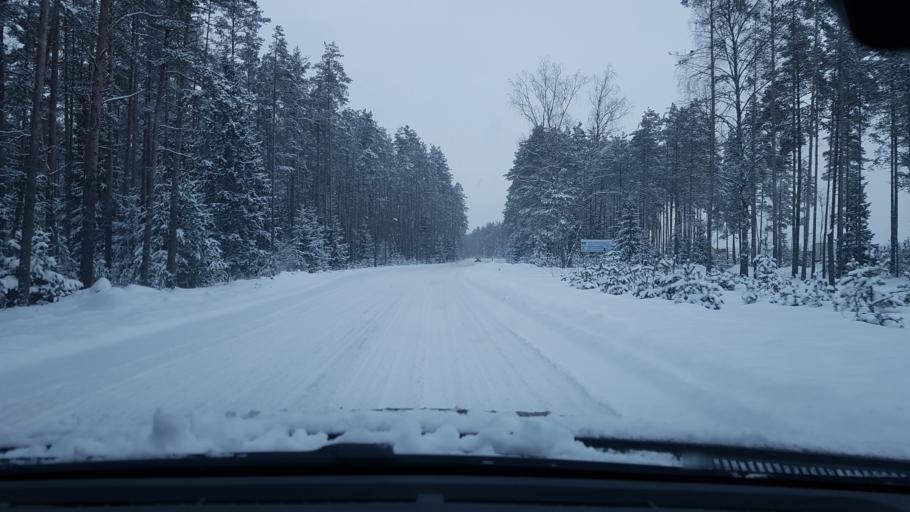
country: EE
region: Harju
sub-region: Anija vald
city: Kehra
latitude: 59.3971
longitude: 25.3722
